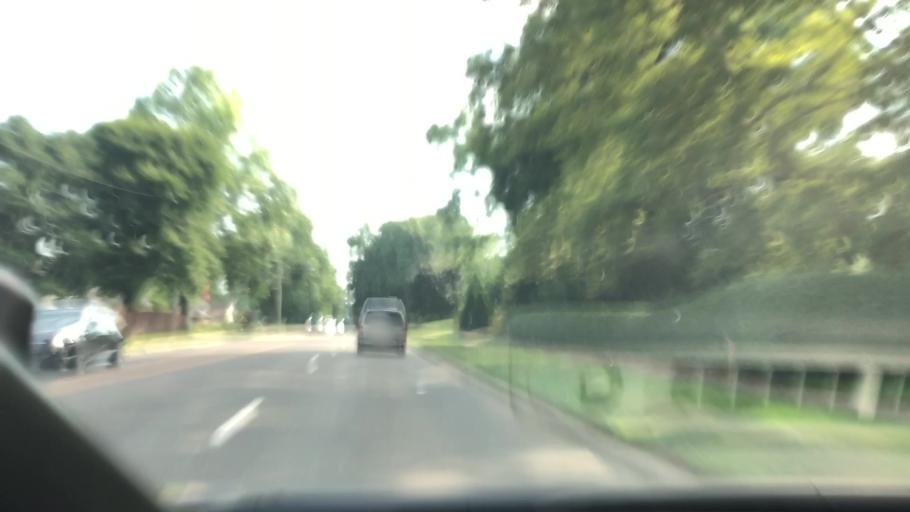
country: US
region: Ohio
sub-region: Stark County
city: Massillon
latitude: 40.8187
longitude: -81.5053
